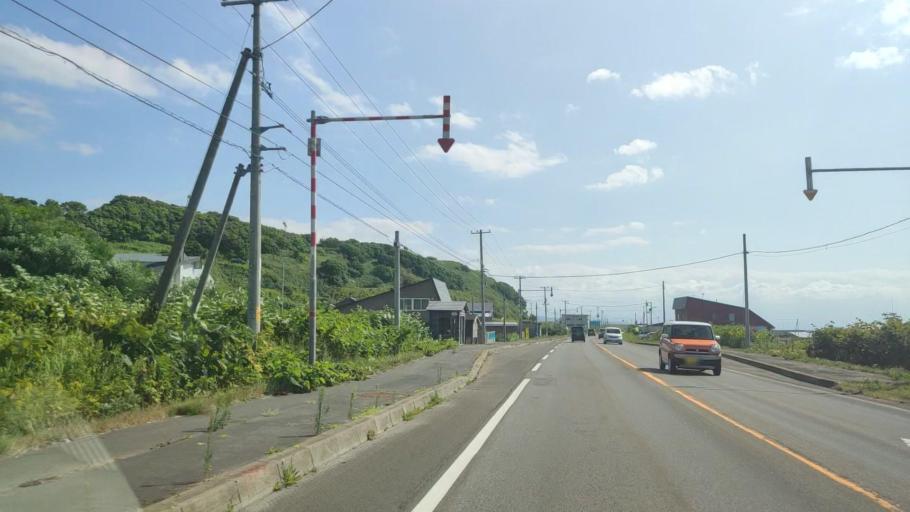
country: JP
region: Hokkaido
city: Rumoi
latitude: 43.9838
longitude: 141.6480
